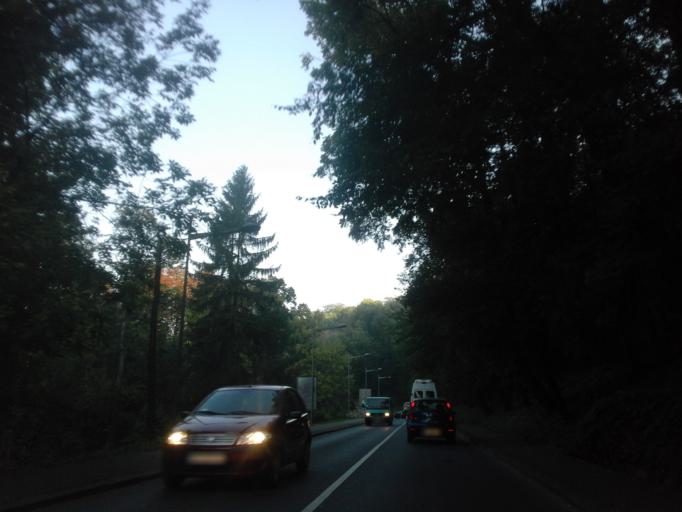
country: RS
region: Central Serbia
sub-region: Belgrade
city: Savski Venac
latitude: 44.7824
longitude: 20.4434
